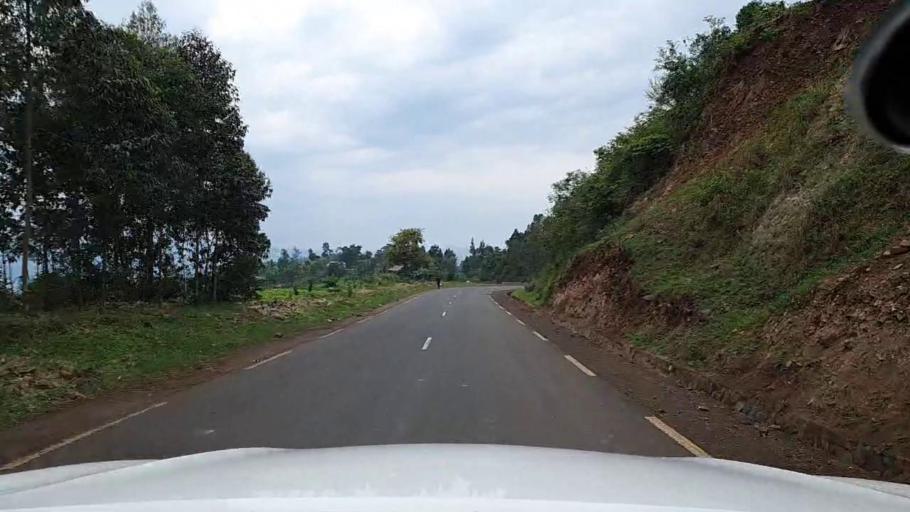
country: RW
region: Western Province
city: Cyangugu
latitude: -2.6557
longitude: 28.9710
